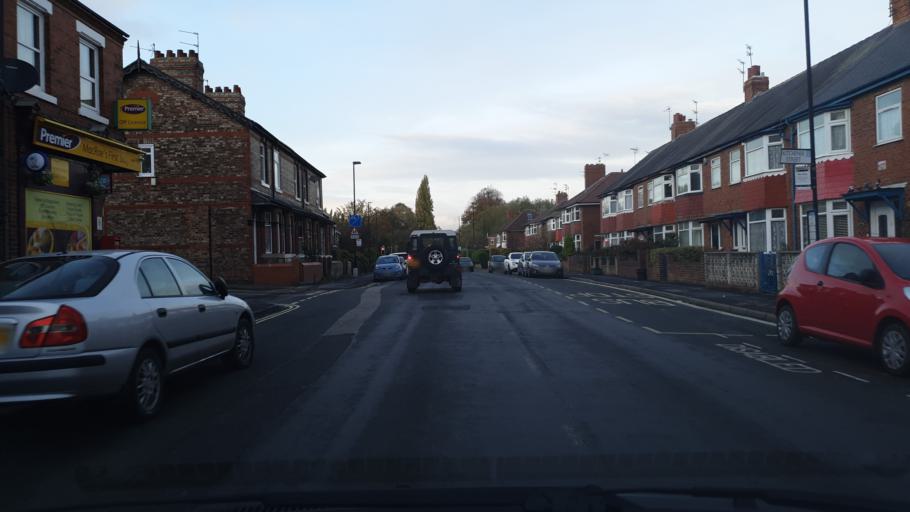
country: GB
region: England
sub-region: City of York
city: York
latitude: 53.9729
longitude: -1.0737
